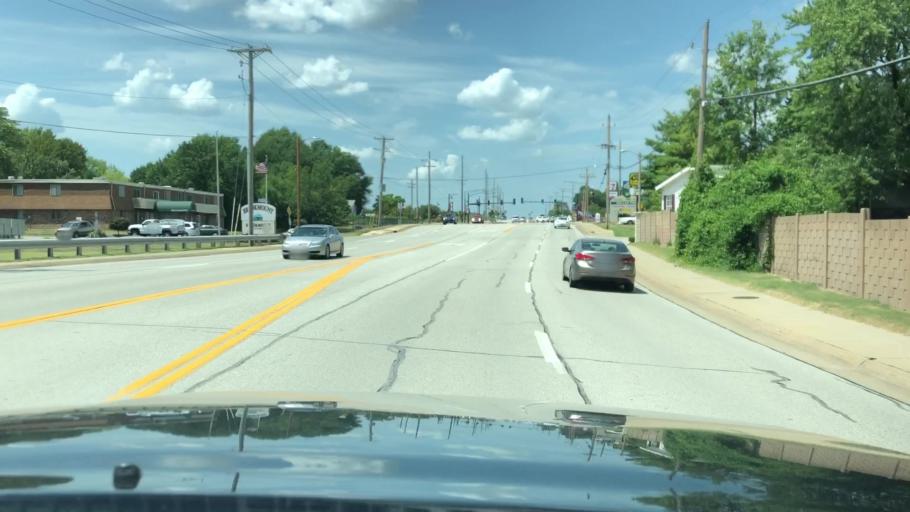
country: US
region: Missouri
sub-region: Saint Charles County
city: Saint Peters
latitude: 38.7882
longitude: -90.6131
